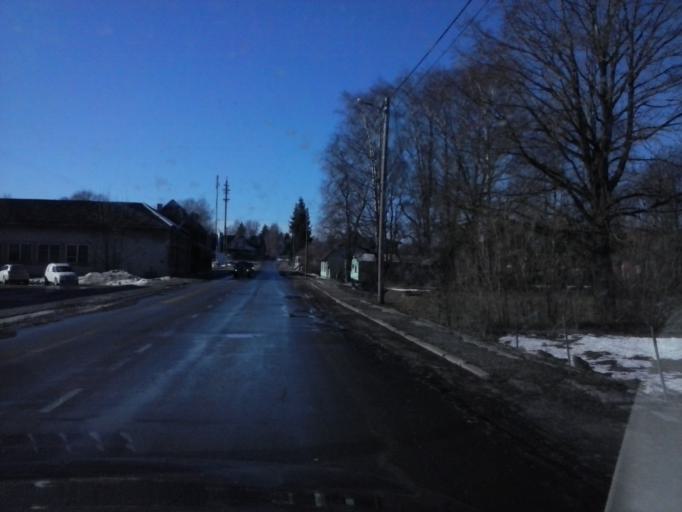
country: EE
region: Jogevamaa
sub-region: Jogeva linn
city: Jogeva
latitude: 58.7404
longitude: 26.3745
